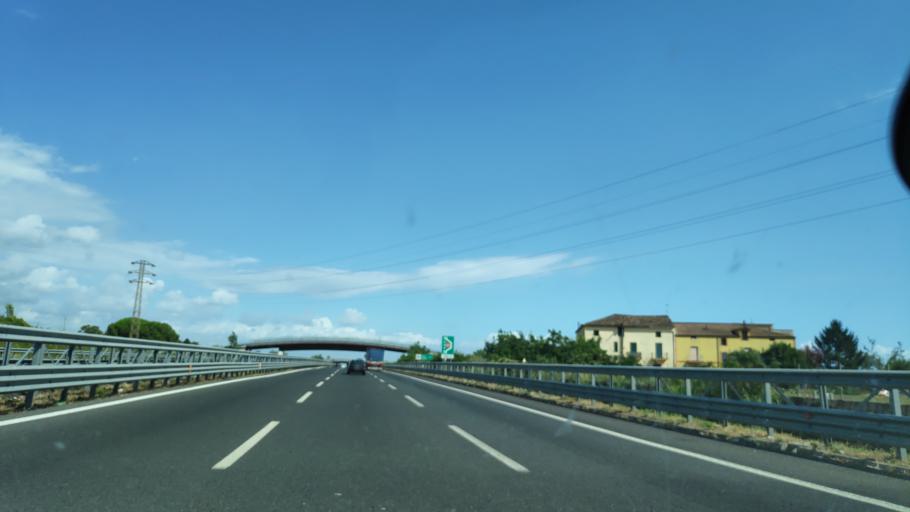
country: IT
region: Campania
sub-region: Provincia di Salerno
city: Pontecagnano
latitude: 40.6494
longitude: 14.8807
